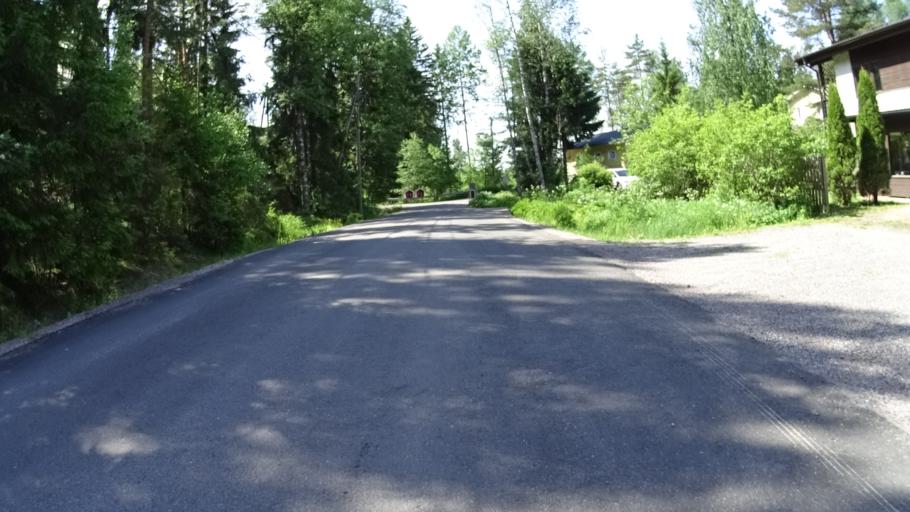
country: FI
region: Uusimaa
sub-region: Helsinki
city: Kauniainen
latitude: 60.3192
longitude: 24.7270
